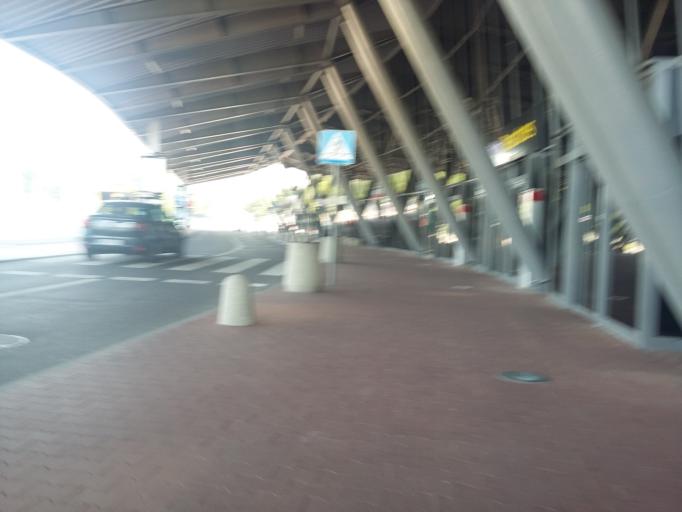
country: PL
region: Lodz Voivodeship
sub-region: Powiat pabianicki
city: Ksawerow
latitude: 51.7272
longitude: 19.4002
